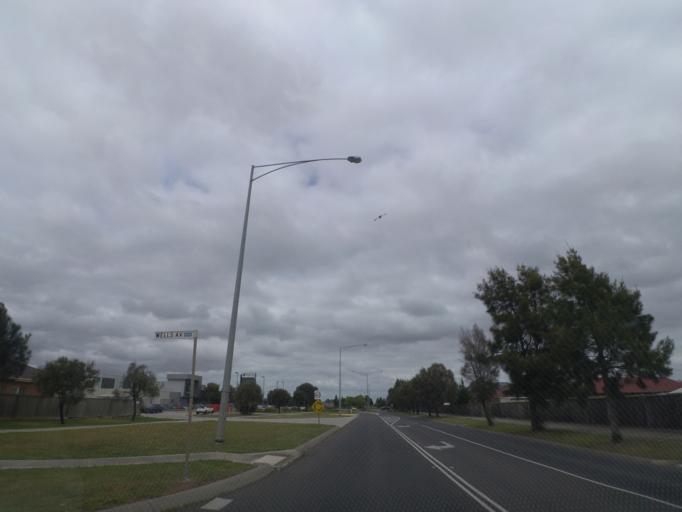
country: AU
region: Victoria
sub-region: Melton
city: Burnside Heights
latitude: -37.7221
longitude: 144.7507
